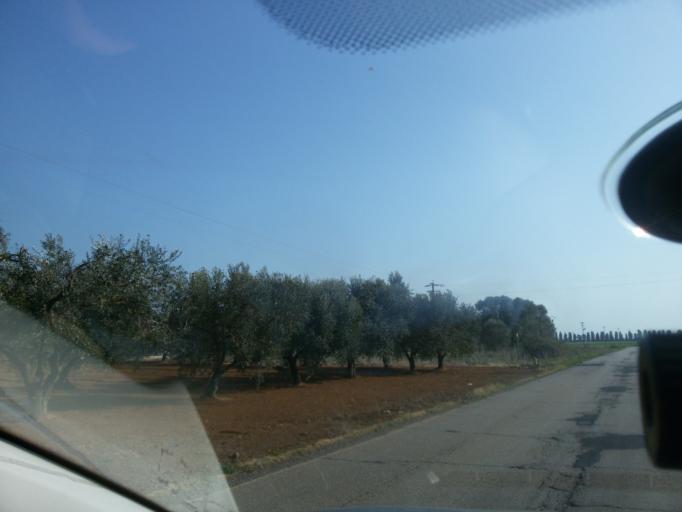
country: IT
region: Apulia
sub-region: Provincia di Brindisi
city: Mesagne
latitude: 40.6043
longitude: 17.8176
